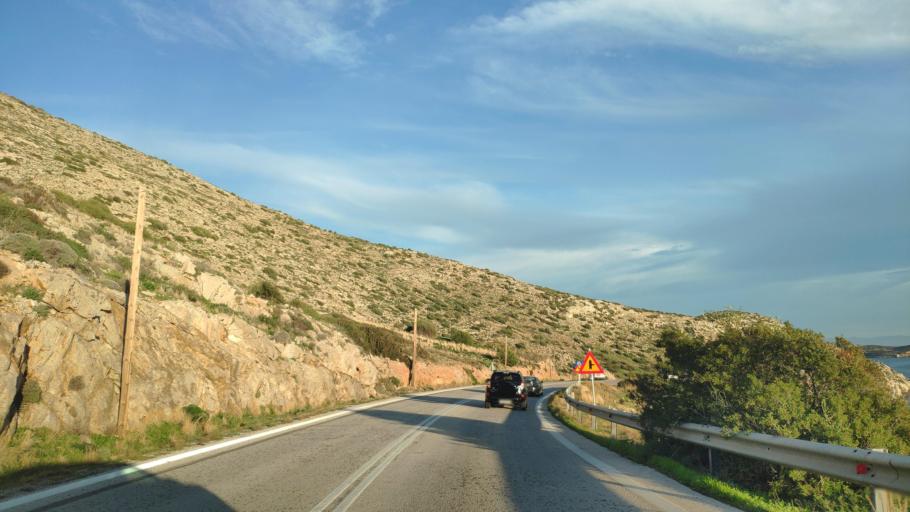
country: GR
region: Attica
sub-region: Nomarchia Anatolikis Attikis
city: Palaia Fokaia
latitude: 37.6712
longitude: 23.9441
